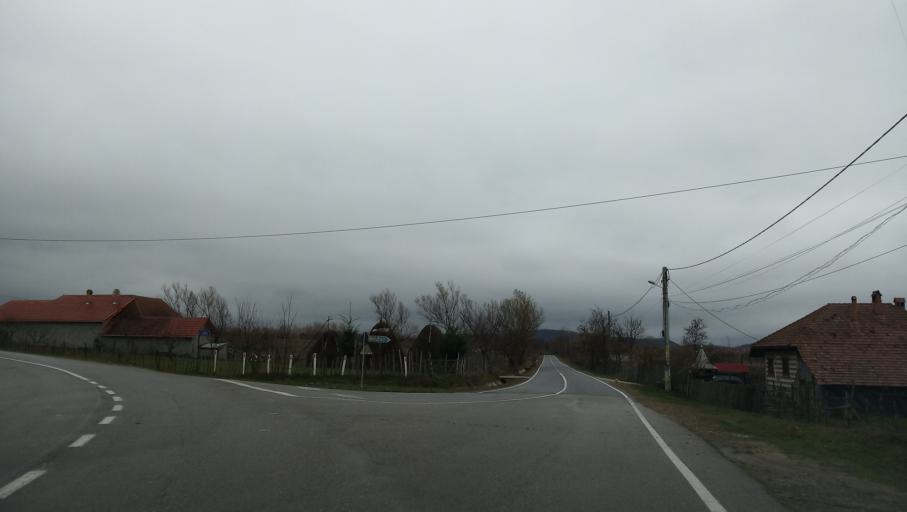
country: RO
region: Gorj
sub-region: Novaci
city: Pociovalistea
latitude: 45.1647
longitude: 23.6134
